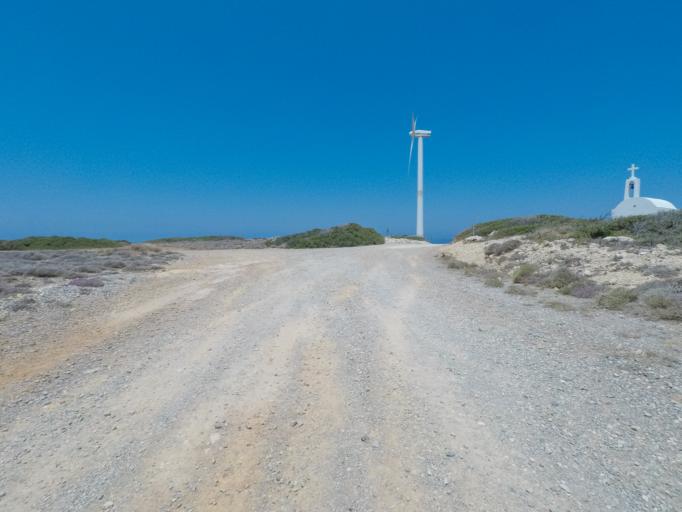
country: GR
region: Crete
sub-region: Nomos Lasithiou
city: Elounda
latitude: 35.3322
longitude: 25.7611
